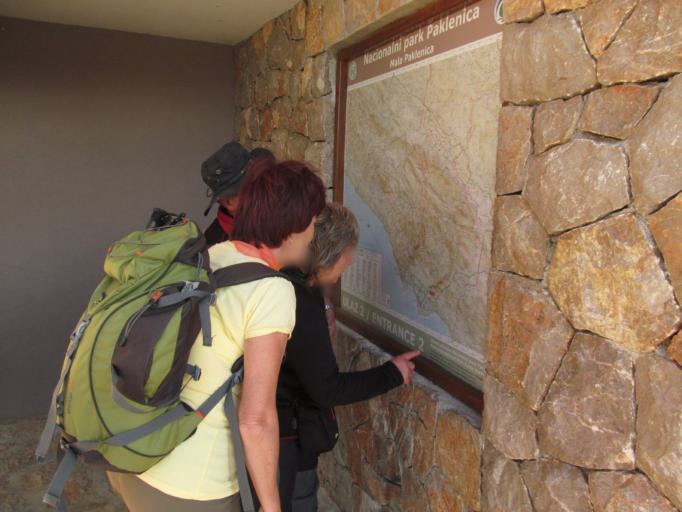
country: HR
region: Zadarska
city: Starigrad
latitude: 44.2831
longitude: 15.4929
